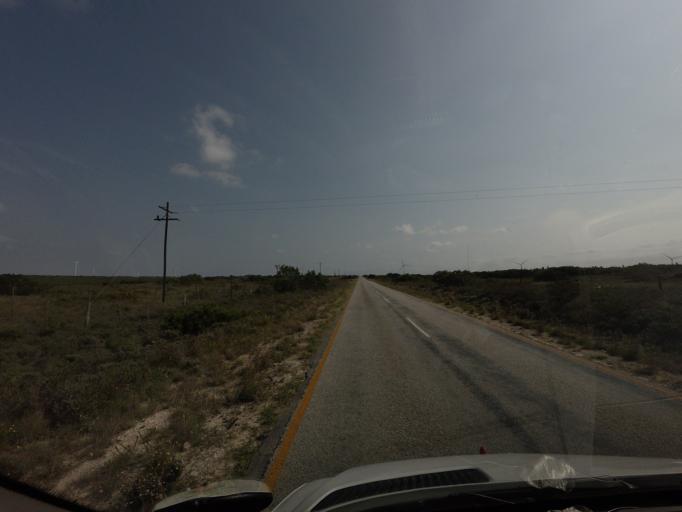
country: ZA
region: Eastern Cape
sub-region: Nelson Mandela Bay Metropolitan Municipality
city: Uitenhage
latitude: -33.6684
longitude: 25.5918
